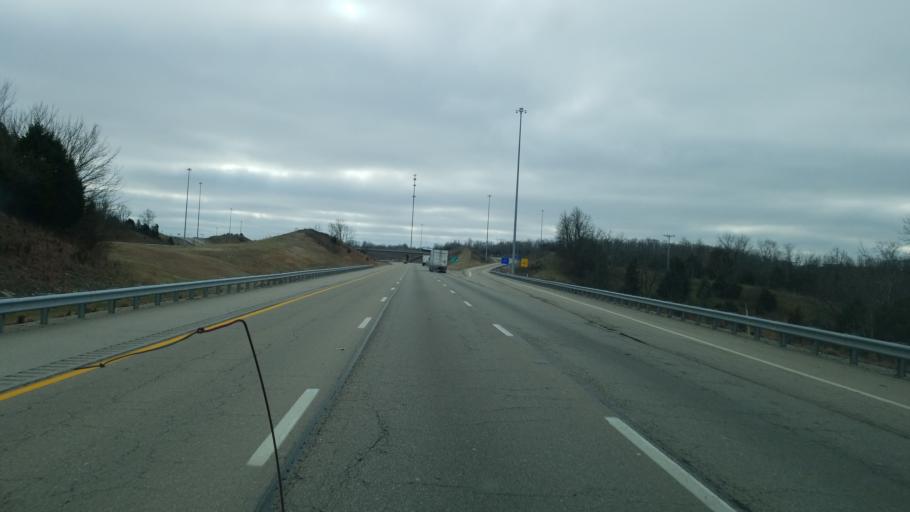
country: US
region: Kentucky
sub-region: Grant County
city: Williamstown
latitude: 38.4948
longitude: -84.5879
